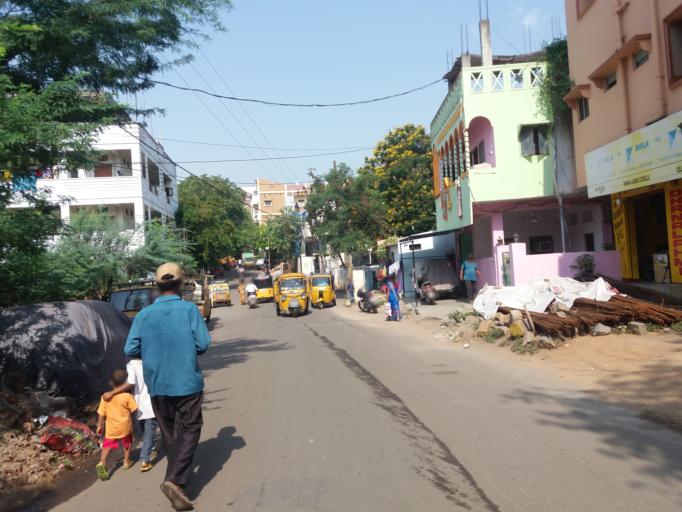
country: IN
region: Telangana
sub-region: Hyderabad
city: Malkajgiri
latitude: 17.4163
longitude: 78.5083
